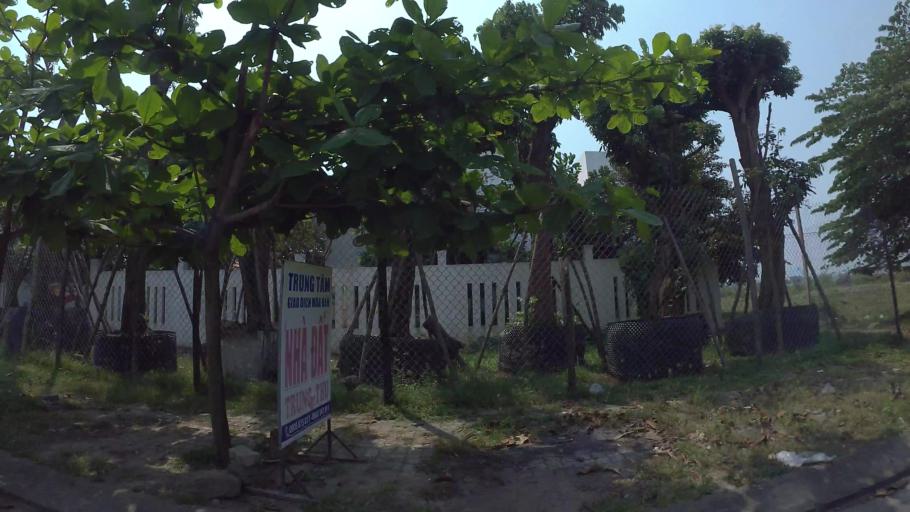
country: VN
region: Da Nang
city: Cam Le
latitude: 15.9793
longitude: 108.2185
